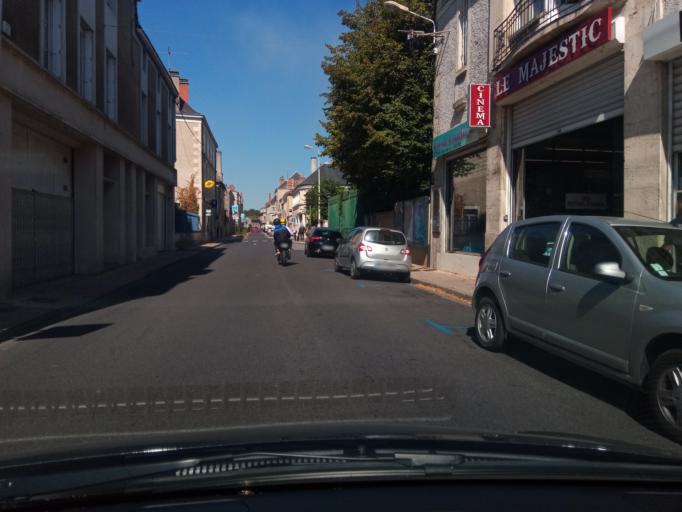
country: FR
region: Poitou-Charentes
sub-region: Departement de la Vienne
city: Montmorillon
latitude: 46.4248
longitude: 0.8701
